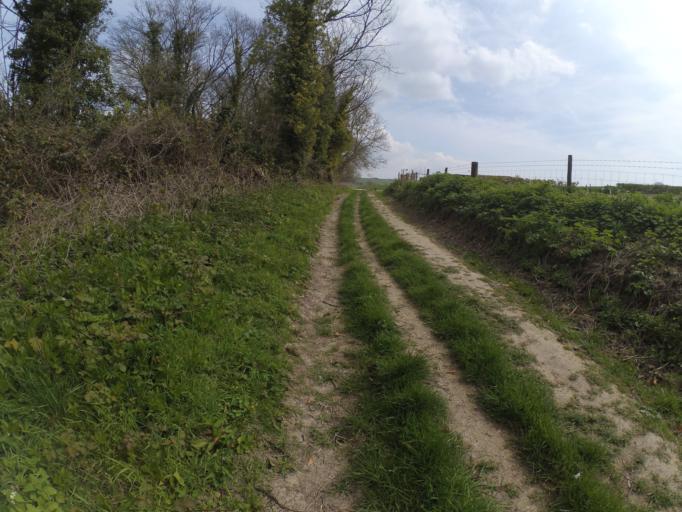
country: GB
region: England
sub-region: West Sussex
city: Arundel
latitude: 50.8798
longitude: -0.5480
